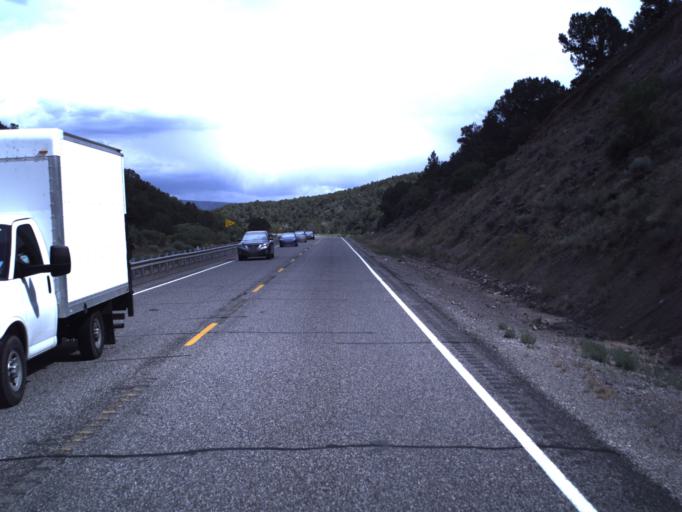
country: US
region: Utah
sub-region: Sevier County
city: Richfield
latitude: 38.7171
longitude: -111.9043
